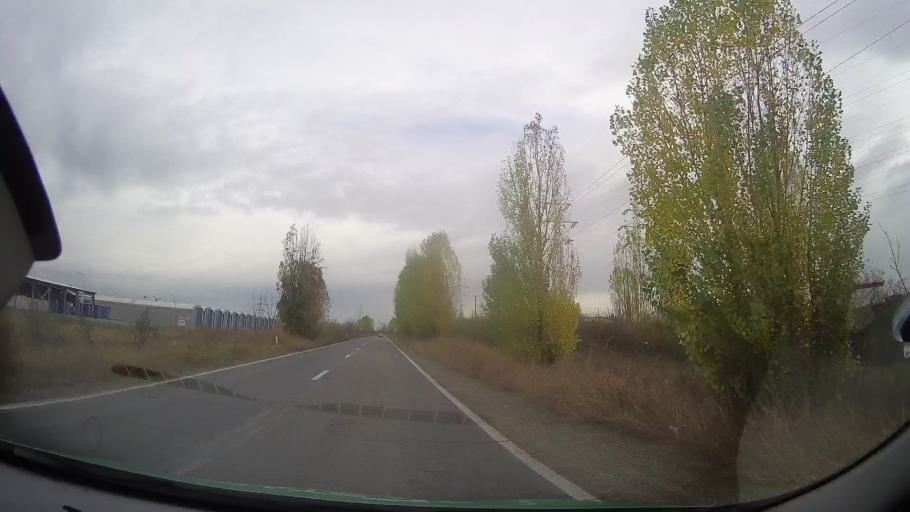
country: RO
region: Prahova
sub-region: Comuna Bucov
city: Bucov
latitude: 44.9542
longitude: 26.0818
